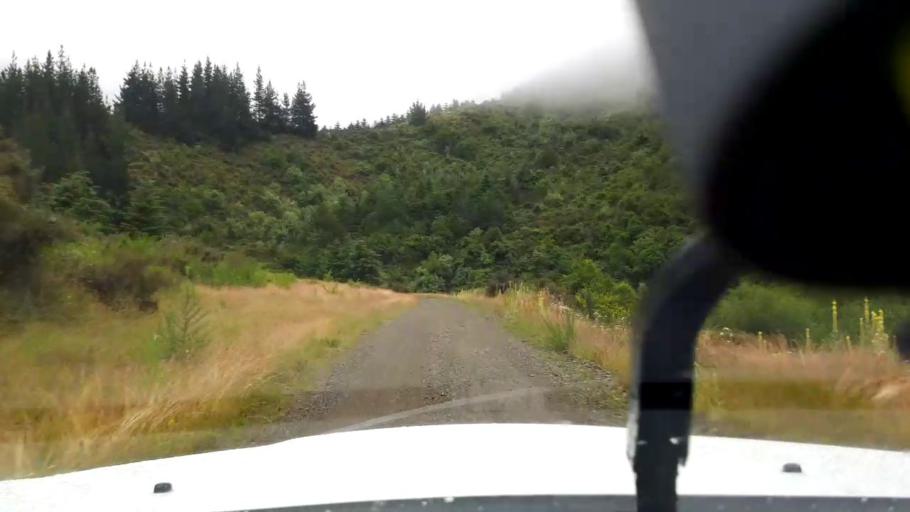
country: NZ
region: Canterbury
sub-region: Timaru District
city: Pleasant Point
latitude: -44.0342
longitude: 171.0059
